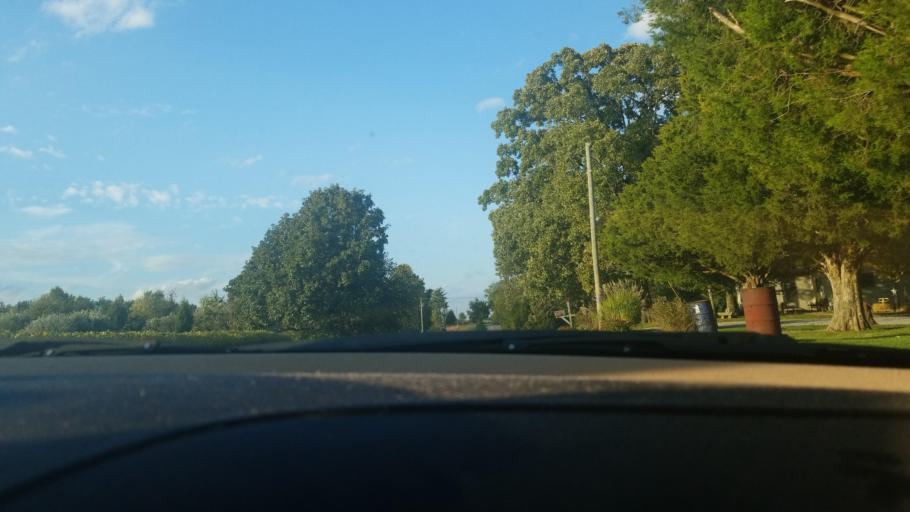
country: US
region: Illinois
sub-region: Saline County
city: Carrier Mills
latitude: 37.7946
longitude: -88.7117
